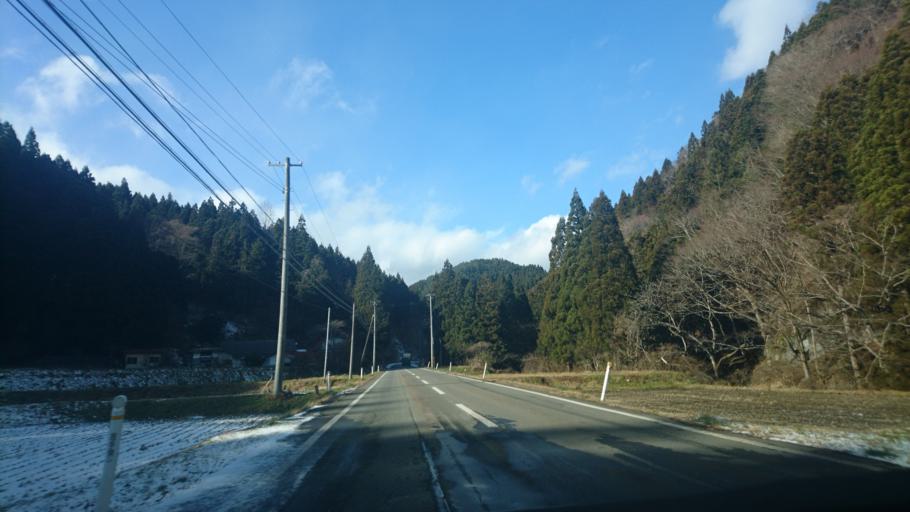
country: JP
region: Iwate
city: Mizusawa
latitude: 39.0850
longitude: 141.3894
